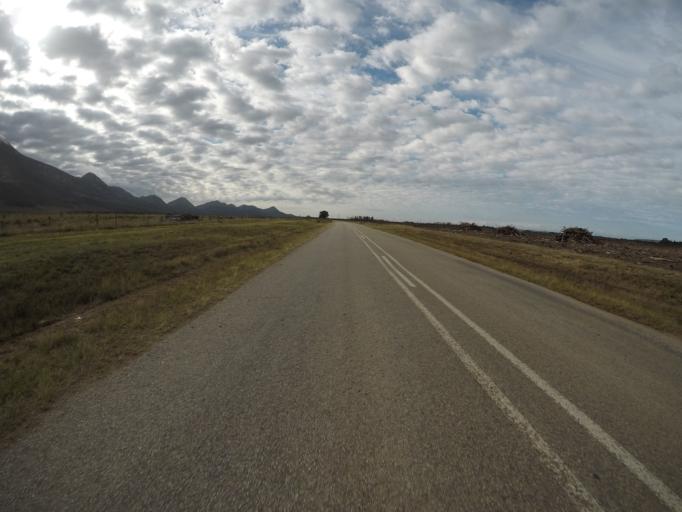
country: ZA
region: Eastern Cape
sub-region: Cacadu District Municipality
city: Kareedouw
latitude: -34.0418
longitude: 24.4118
